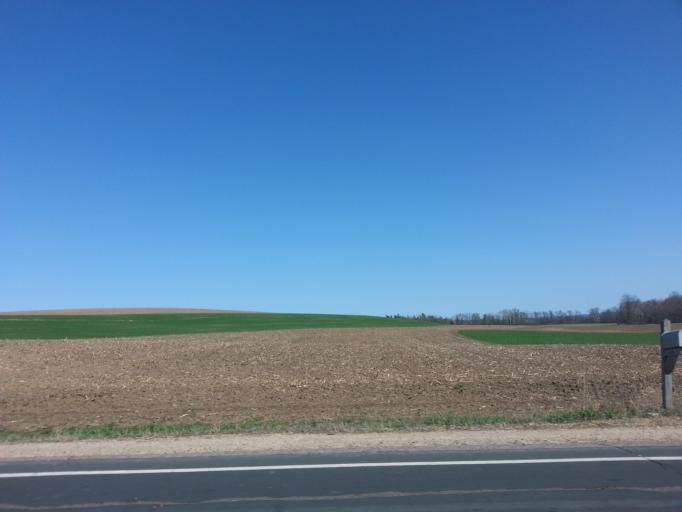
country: US
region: Wisconsin
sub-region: Pepin County
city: Durand
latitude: 44.6899
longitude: -91.9487
